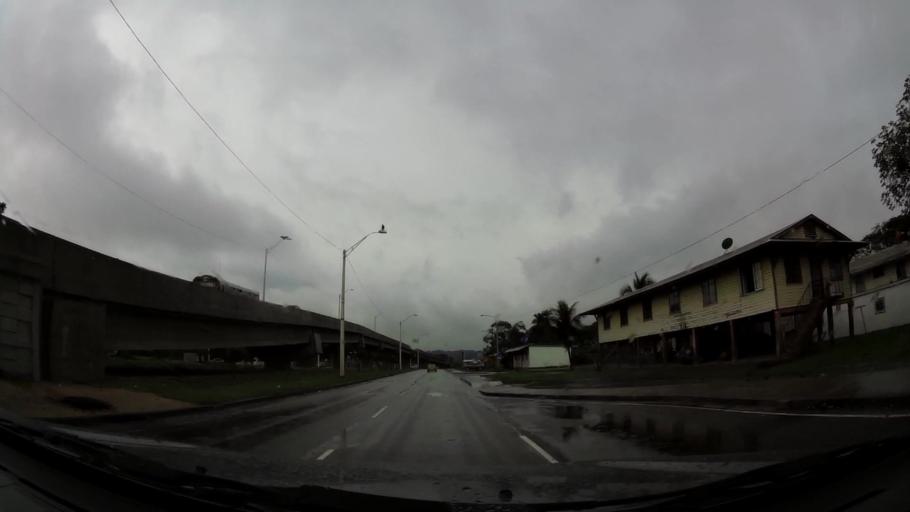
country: PA
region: Colon
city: Arco Iris
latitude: 9.3376
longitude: -79.8896
